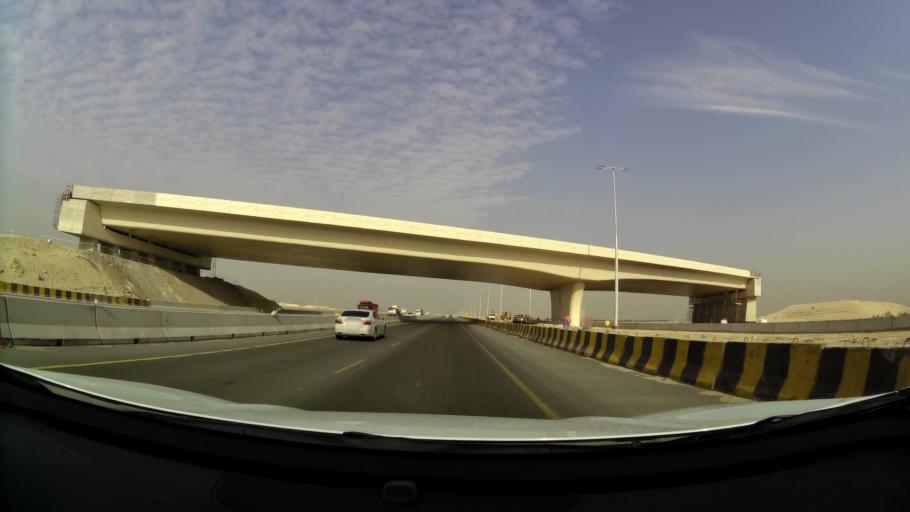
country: AE
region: Abu Dhabi
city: Abu Dhabi
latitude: 24.2780
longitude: 54.5235
